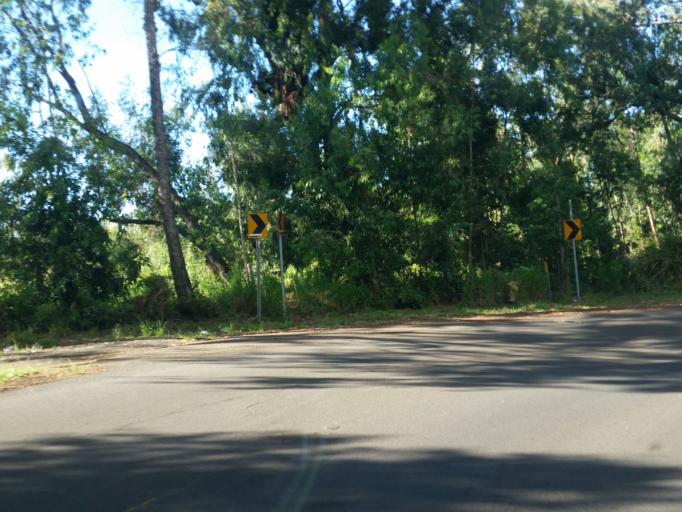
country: US
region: Hawaii
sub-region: Maui County
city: Pukalani
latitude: 20.8307
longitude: -156.3163
